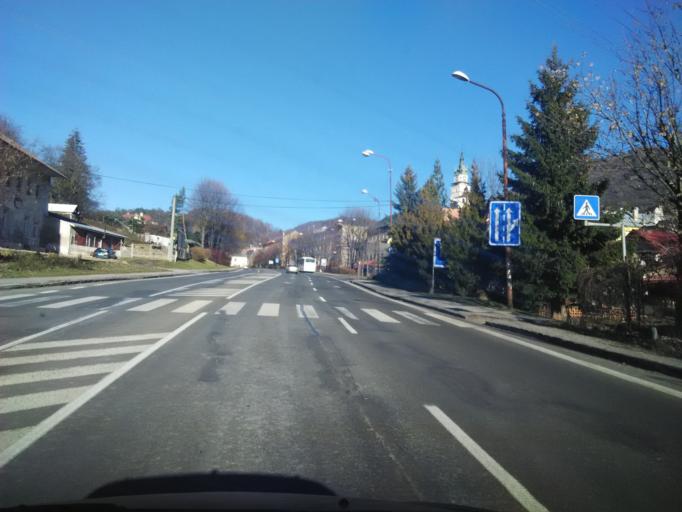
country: SK
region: Banskobystricky
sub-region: Okres Ziar nad Hronom
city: Kremnica
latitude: 48.7027
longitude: 18.9151
